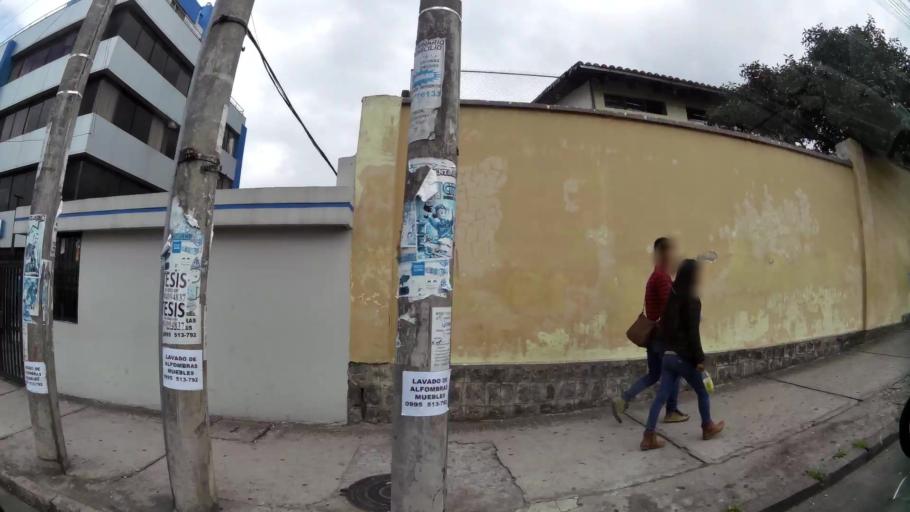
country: EC
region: Pichincha
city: Quito
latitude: -0.1395
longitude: -78.4964
